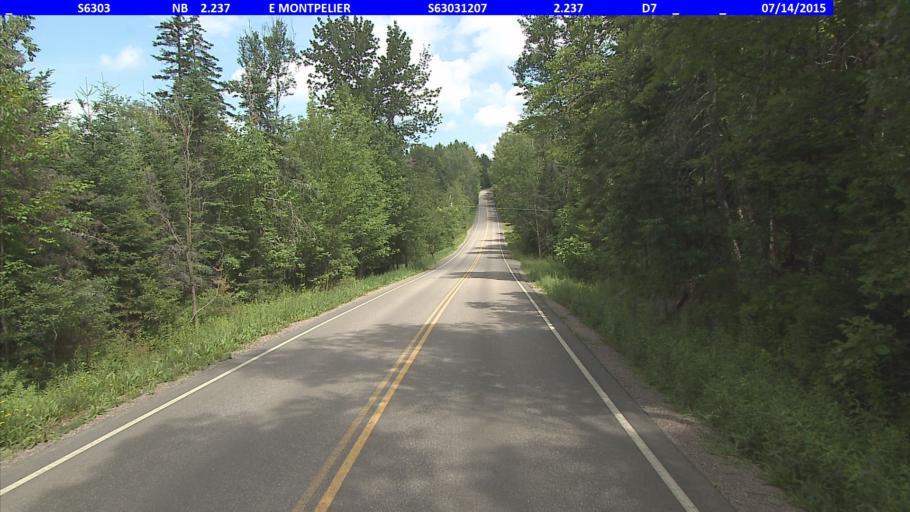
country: US
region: Vermont
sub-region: Washington County
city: Montpelier
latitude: 44.3004
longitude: -72.5345
